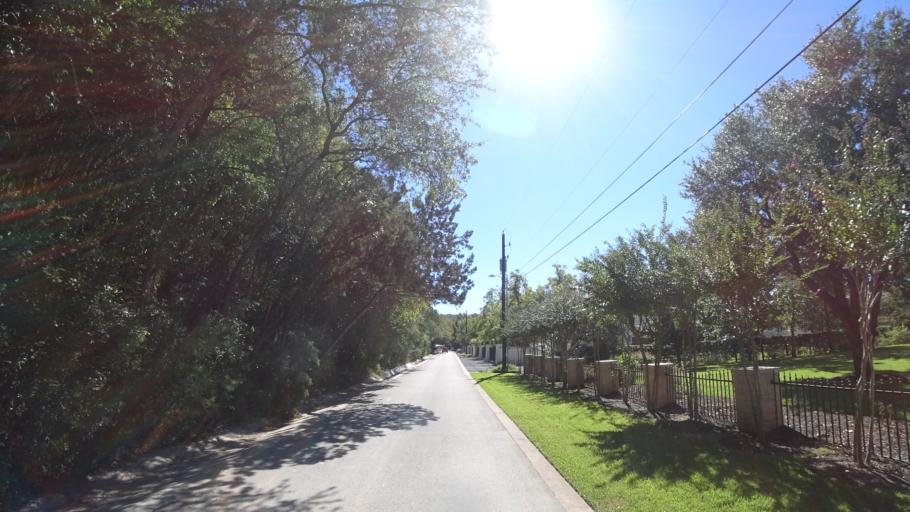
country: US
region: Texas
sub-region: Travis County
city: West Lake Hills
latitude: 30.3354
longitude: -97.7808
